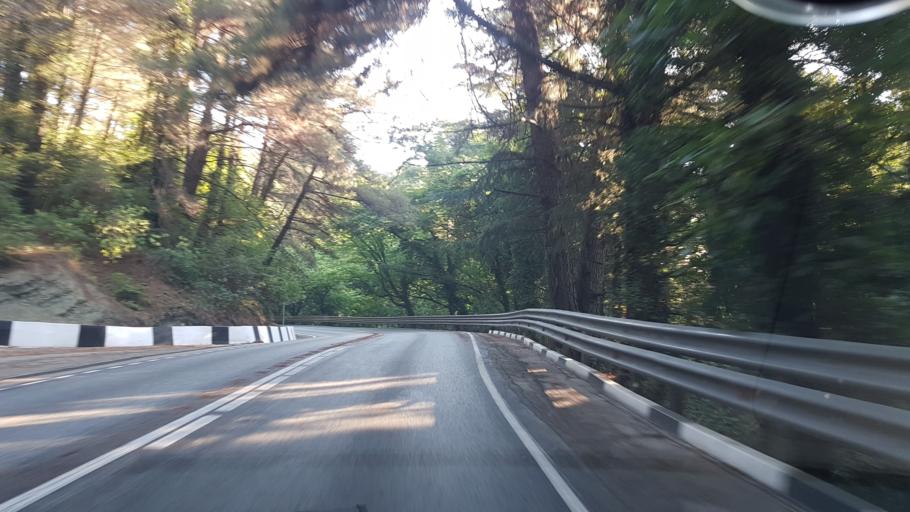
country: RU
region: Krasnodarskiy
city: Gornoye Loo
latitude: 43.6680
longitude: 39.6151
